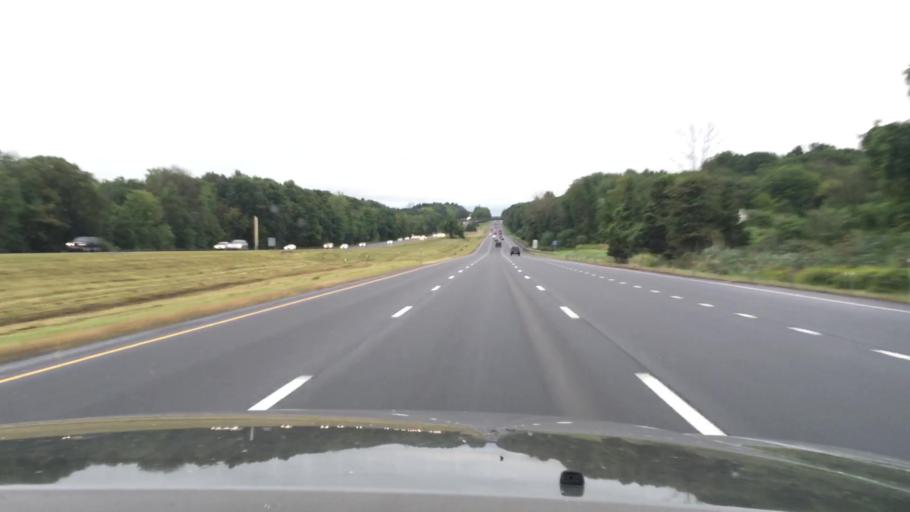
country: US
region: Connecticut
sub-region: New Haven County
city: Wallingford Center
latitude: 41.4774
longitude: -72.7713
